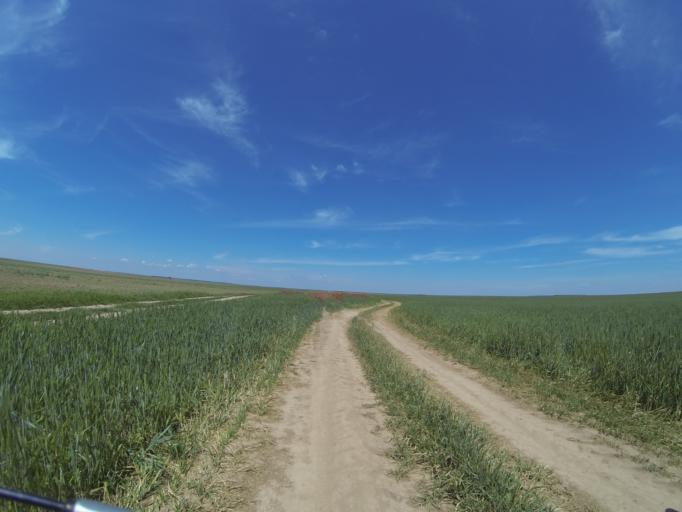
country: RO
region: Dolj
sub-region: Comuna Teslui
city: Teslui
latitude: 44.1817
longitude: 24.1714
